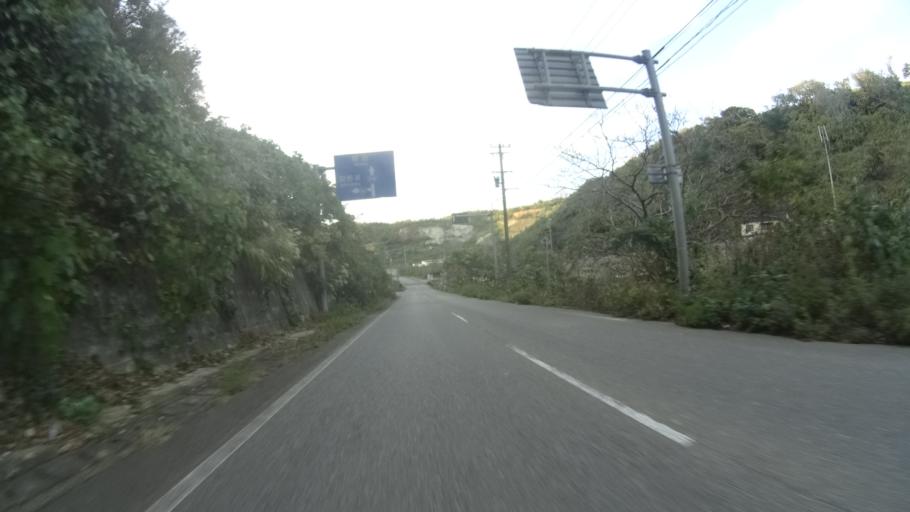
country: JP
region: Ishikawa
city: Nanao
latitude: 37.2179
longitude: 136.7002
